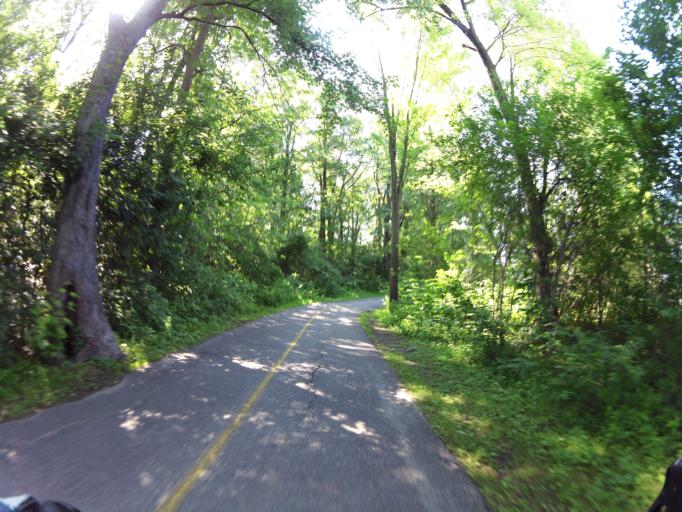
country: CA
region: Quebec
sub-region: Outaouais
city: Gatineau
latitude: 45.4506
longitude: -75.7192
